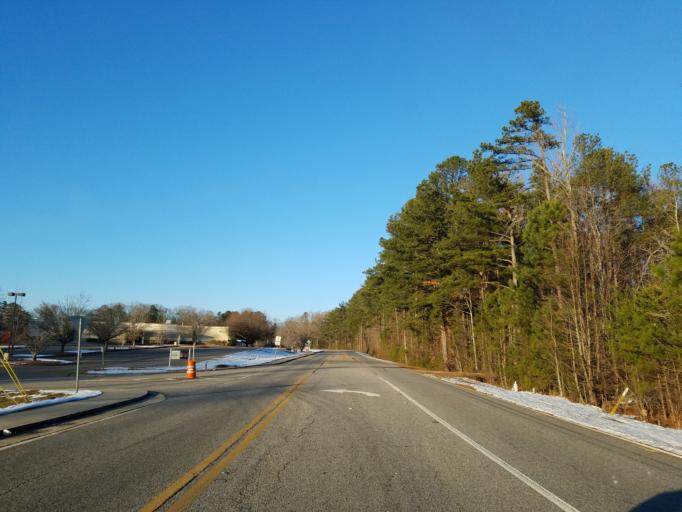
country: US
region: Georgia
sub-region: Dawson County
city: Dawsonville
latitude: 34.4189
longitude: -84.1045
